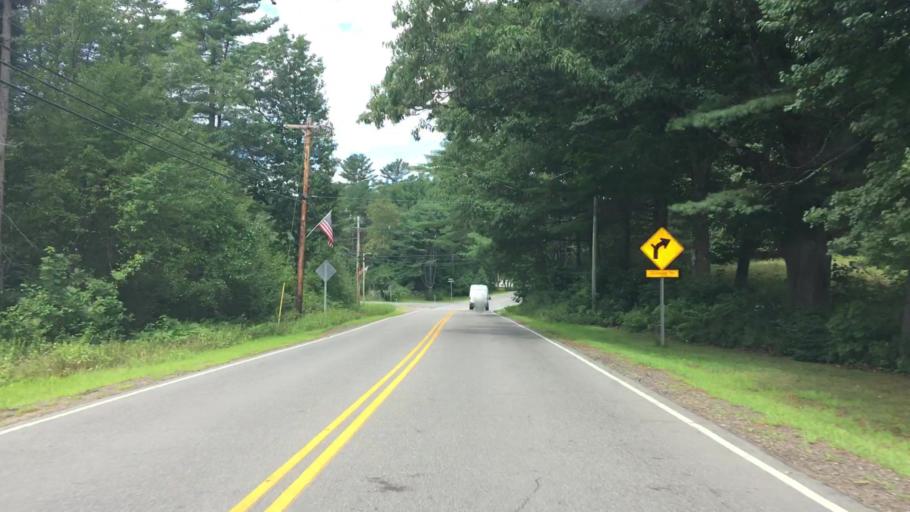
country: US
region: New Hampshire
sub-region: Belknap County
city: Meredith
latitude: 43.6153
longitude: -71.5357
